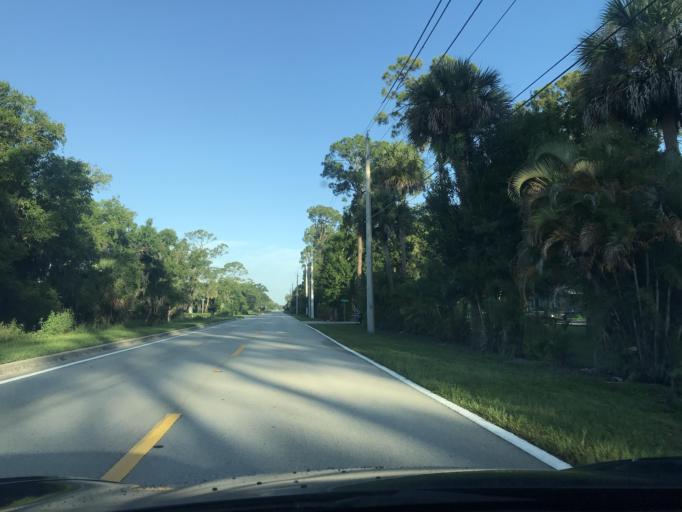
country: US
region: Florida
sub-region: Indian River County
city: West Vero Corridor
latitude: 27.6607
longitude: -80.4514
